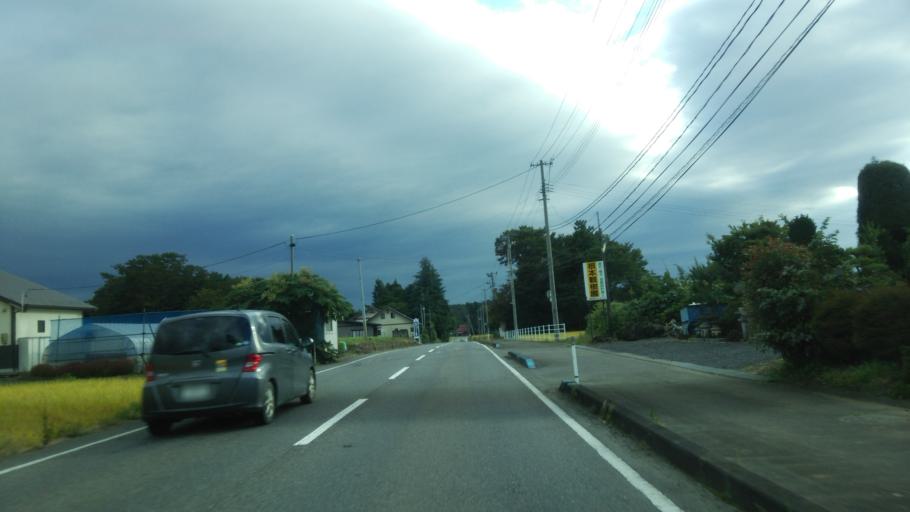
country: JP
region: Fukushima
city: Sukagawa
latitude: 37.3143
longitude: 140.2912
